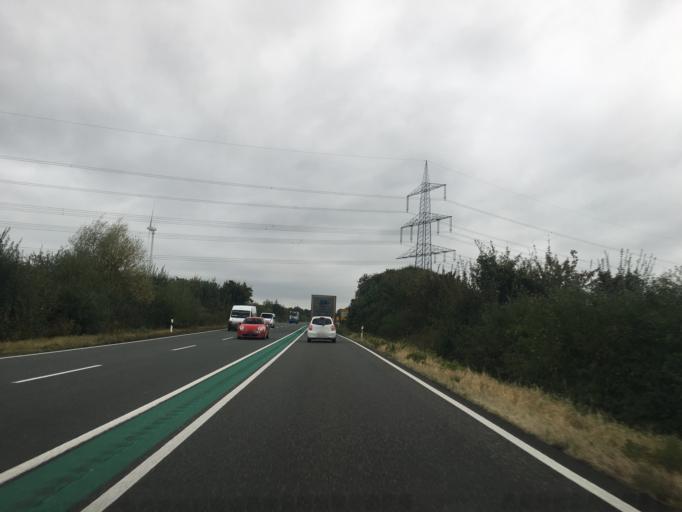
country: DE
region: North Rhine-Westphalia
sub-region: Regierungsbezirk Munster
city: Altenberge
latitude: 52.0760
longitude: 7.4255
